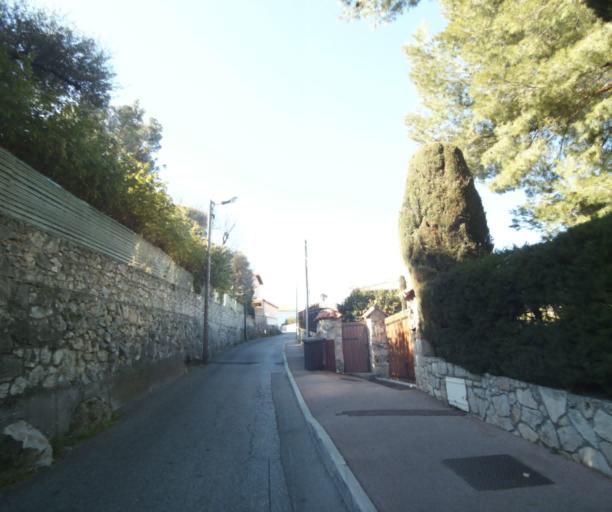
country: FR
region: Provence-Alpes-Cote d'Azur
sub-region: Departement des Alpes-Maritimes
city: Antibes
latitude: 43.5749
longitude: 7.1201
